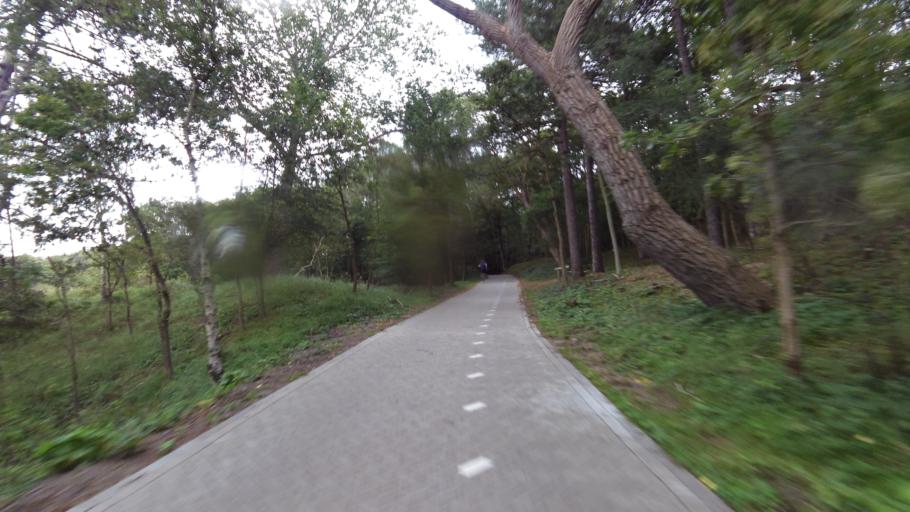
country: NL
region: North Holland
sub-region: Gemeente Bloemendaal
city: Bloemendaal
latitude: 52.4335
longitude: 4.6162
